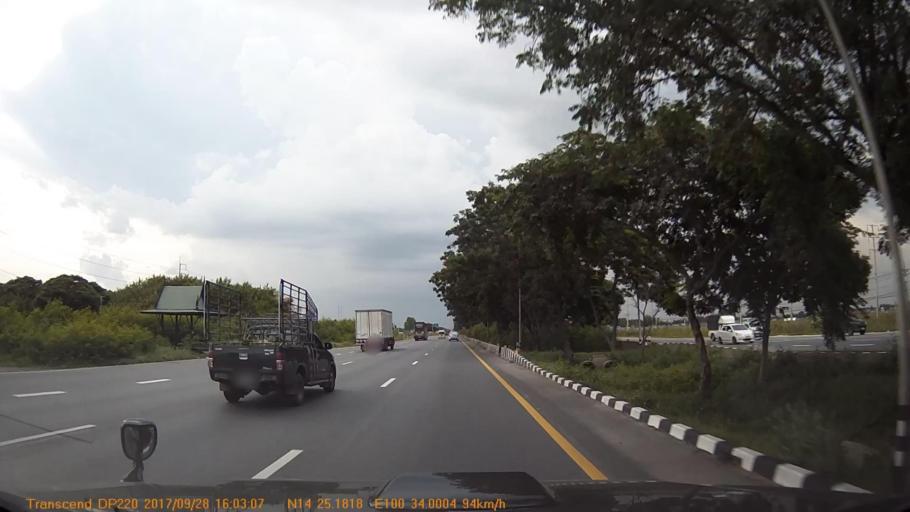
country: TH
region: Phra Nakhon Si Ayutthaya
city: Bang Pahan
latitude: 14.4200
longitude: 100.5663
